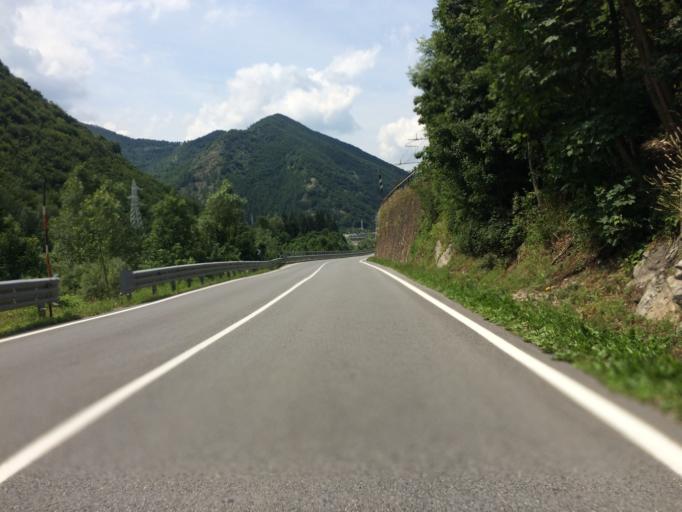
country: IT
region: Piedmont
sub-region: Provincia di Cuneo
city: Vernante
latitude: 44.2378
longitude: 7.5425
